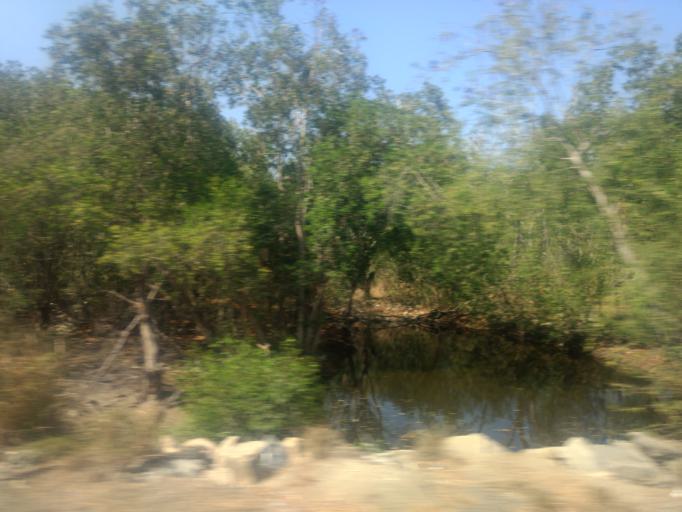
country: MX
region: Colima
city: El Colomo
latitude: 19.0490
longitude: -104.2650
